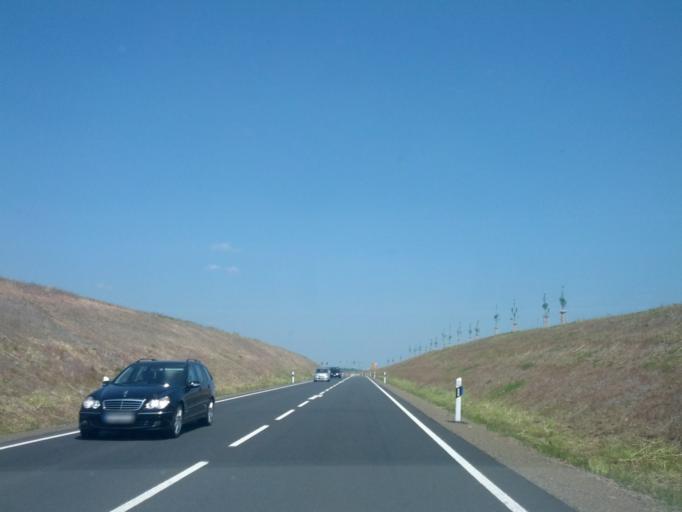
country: DE
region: Thuringia
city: Ernstroda
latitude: 50.9135
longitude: 10.6463
